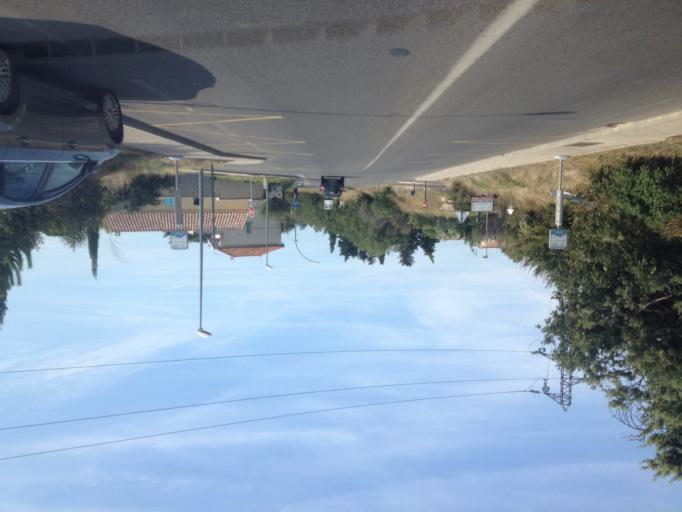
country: FR
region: Provence-Alpes-Cote d'Azur
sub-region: Departement du Vaucluse
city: Carpentras
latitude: 44.0654
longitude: 5.0454
